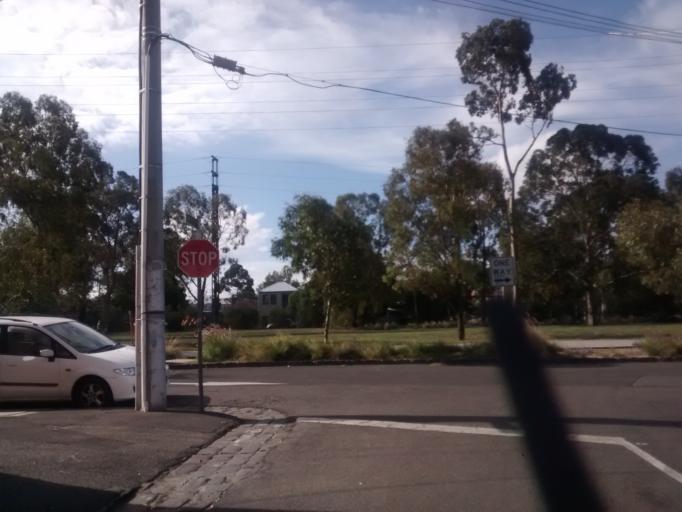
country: AU
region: Victoria
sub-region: Yarra
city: North Fitzroy
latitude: -37.7812
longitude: 144.9843
